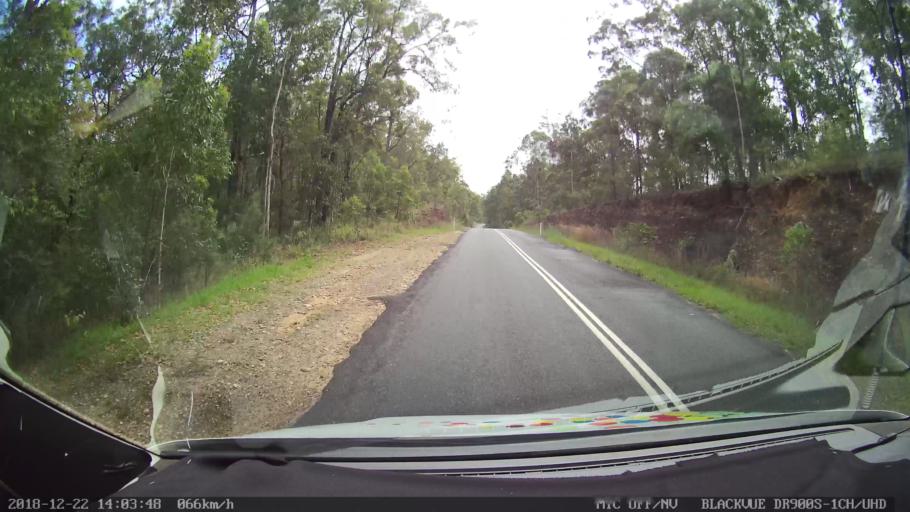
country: AU
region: New South Wales
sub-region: Clarence Valley
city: Coutts Crossing
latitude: -29.9320
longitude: 152.7348
